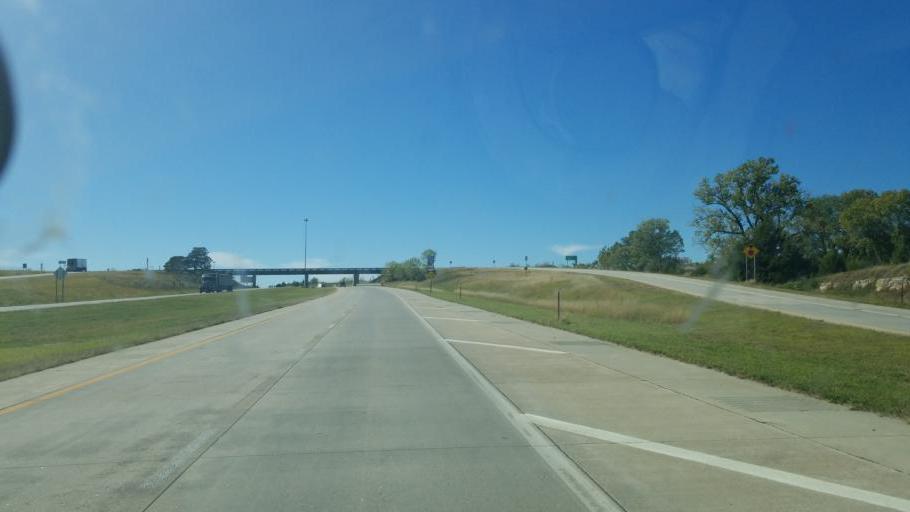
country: US
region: Kansas
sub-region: Geary County
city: Grandview Plaza
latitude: 39.0603
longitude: -96.7386
